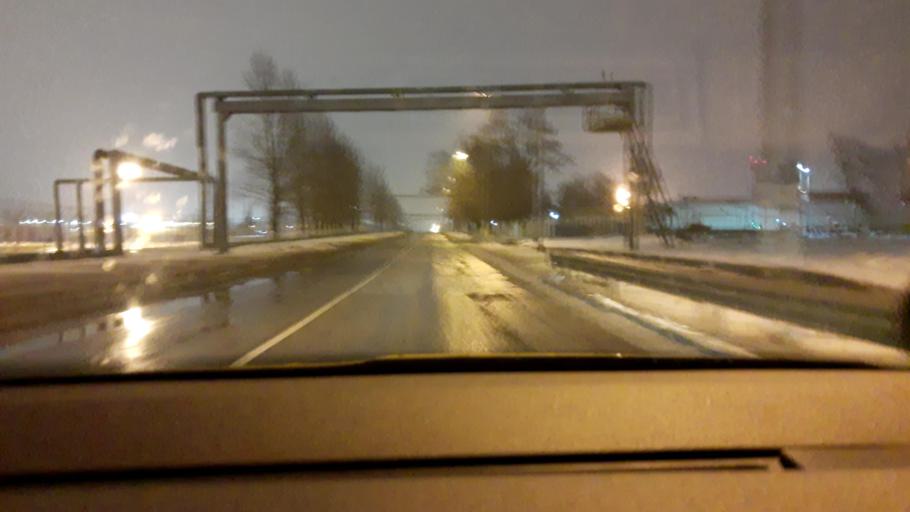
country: RU
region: Moskovskaya
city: Yakovlevskoye
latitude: 55.4293
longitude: 37.8755
